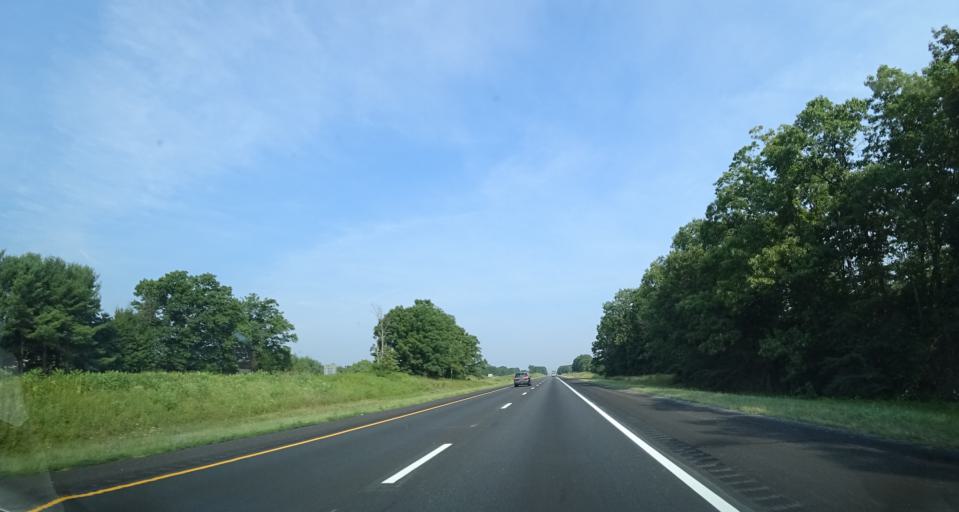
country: US
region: Virginia
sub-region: Warren County
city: Front Royal
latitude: 38.9753
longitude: -78.2163
